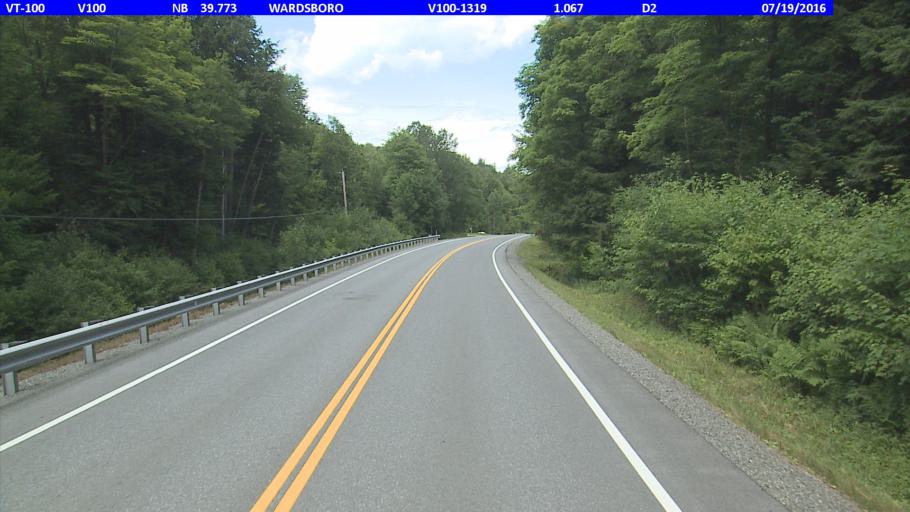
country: US
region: Vermont
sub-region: Windham County
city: Dover
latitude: 43.0150
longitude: -72.8613
